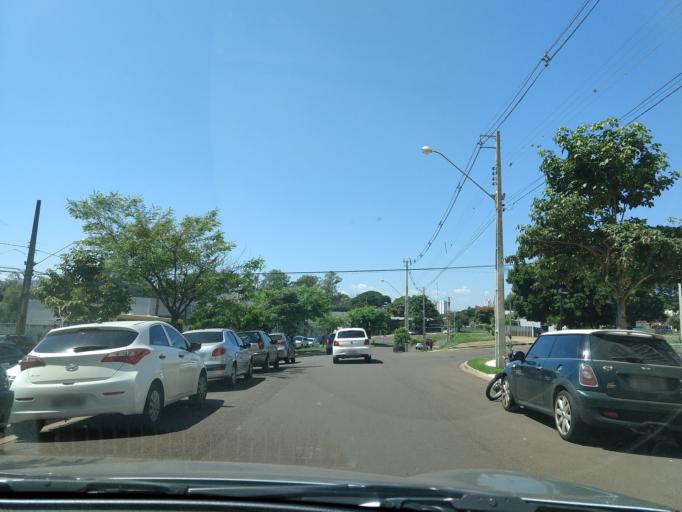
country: BR
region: Parana
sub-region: Londrina
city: Londrina
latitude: -23.3306
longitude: -51.1735
